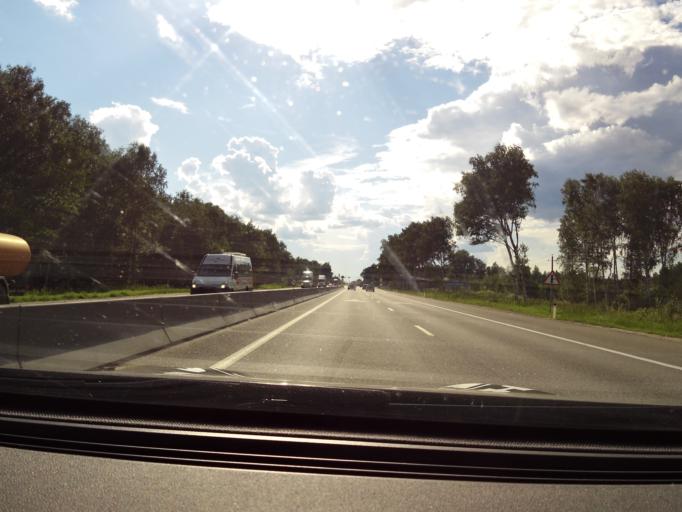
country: RU
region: Nizjnij Novgorod
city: Babino
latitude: 56.3050
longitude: 43.6377
